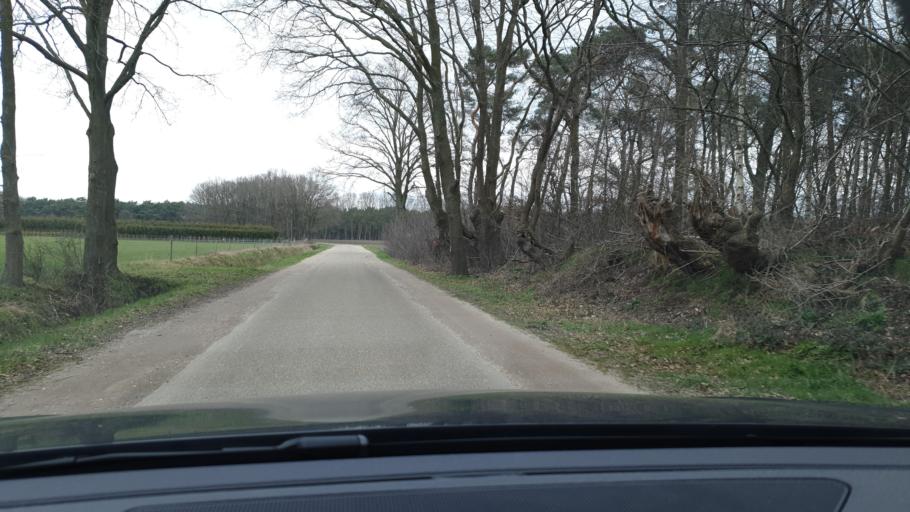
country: NL
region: North Brabant
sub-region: Gemeente Veldhoven
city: Oerle
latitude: 51.4182
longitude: 5.3503
